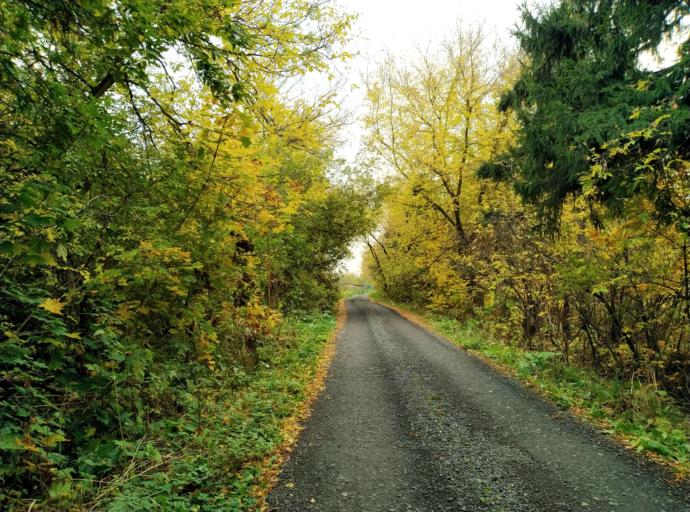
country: RU
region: Moskovskaya
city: Bol'shiye Vyazemy
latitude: 55.6434
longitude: 36.9798
